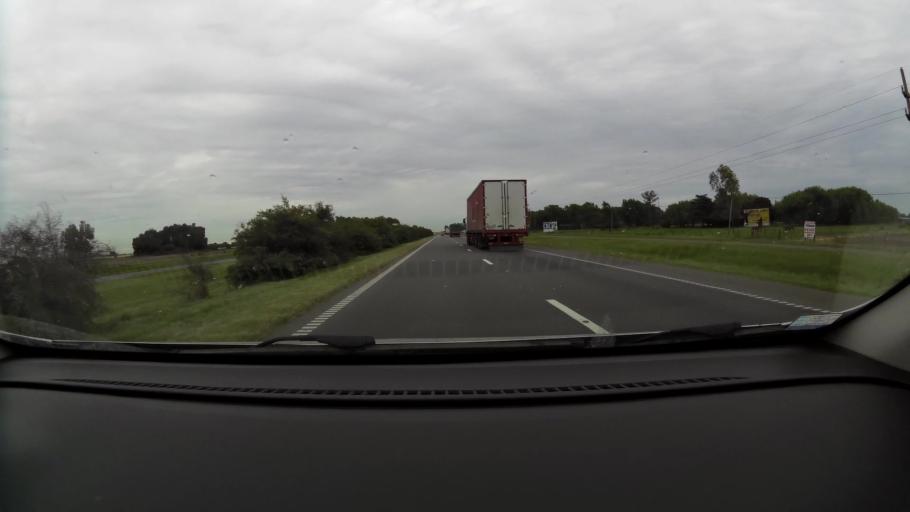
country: AR
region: Buenos Aires
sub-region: Partido de Zarate
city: Zarate
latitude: -34.0882
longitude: -59.1873
